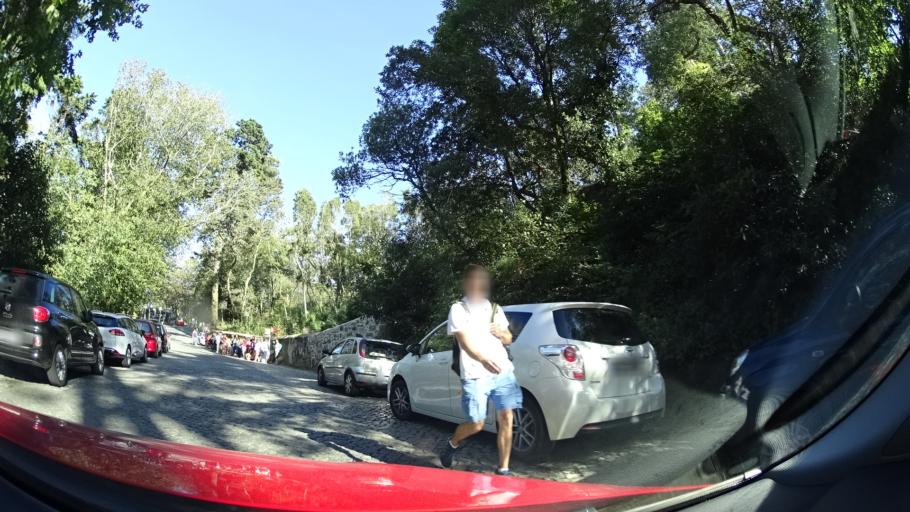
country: PT
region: Lisbon
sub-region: Sintra
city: Sintra
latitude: 38.7899
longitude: -9.3905
